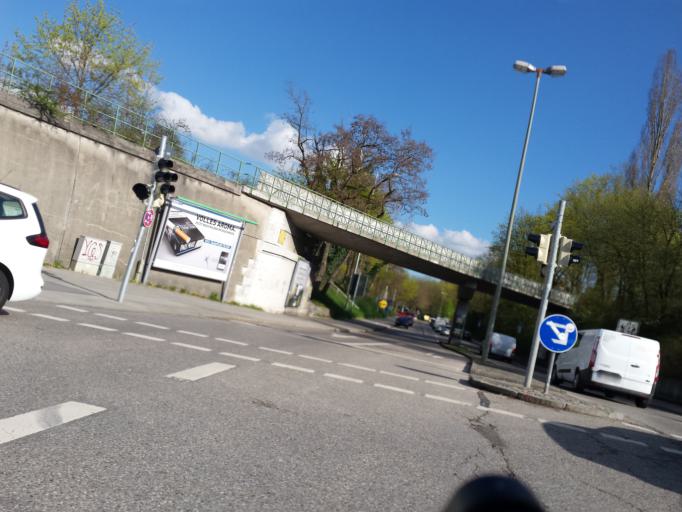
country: DE
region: Bavaria
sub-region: Upper Bavaria
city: Munich
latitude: 48.1202
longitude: 11.5558
